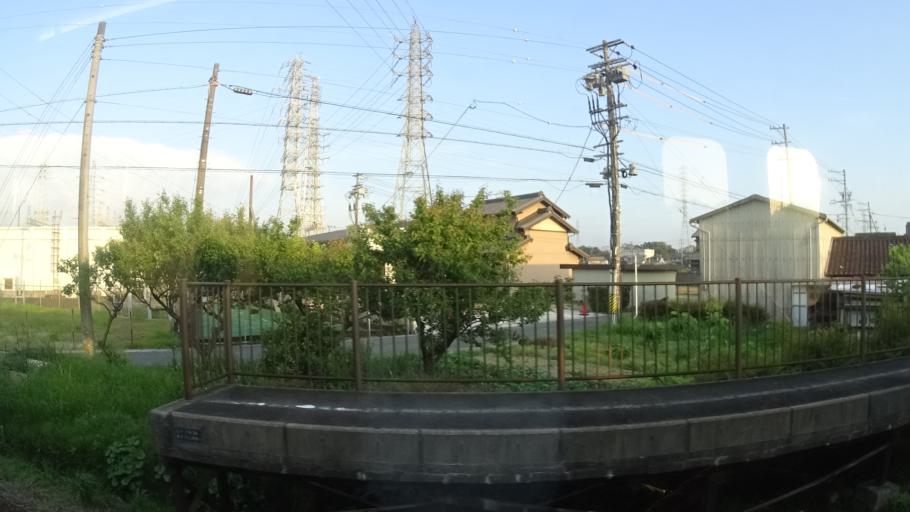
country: JP
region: Aichi
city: Toyohashi
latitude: 34.7113
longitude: 137.3736
